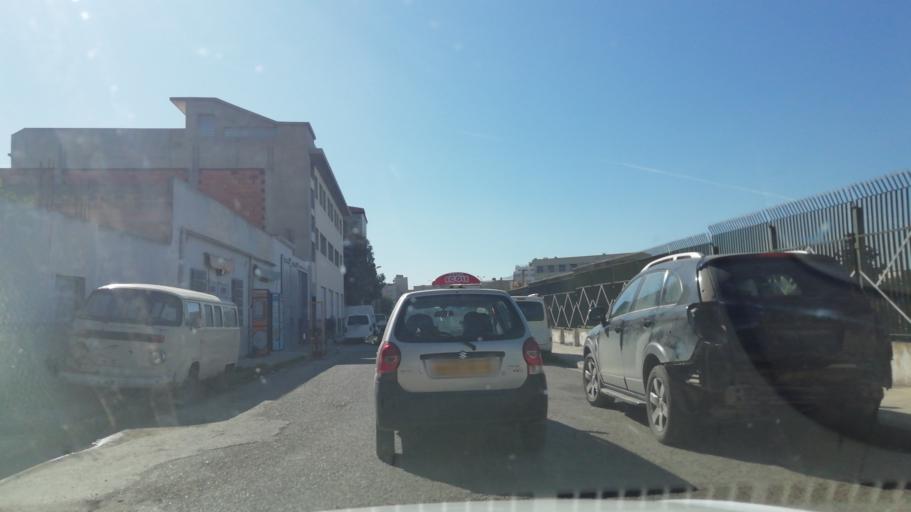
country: DZ
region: Oran
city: Oran
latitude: 35.6973
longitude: -0.6286
